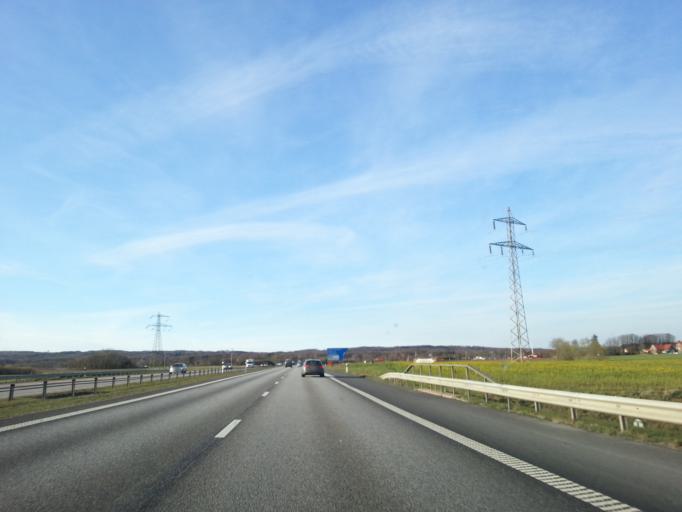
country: SE
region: Skane
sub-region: Angelholms Kommun
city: AEngelholm
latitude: 56.3088
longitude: 12.9097
